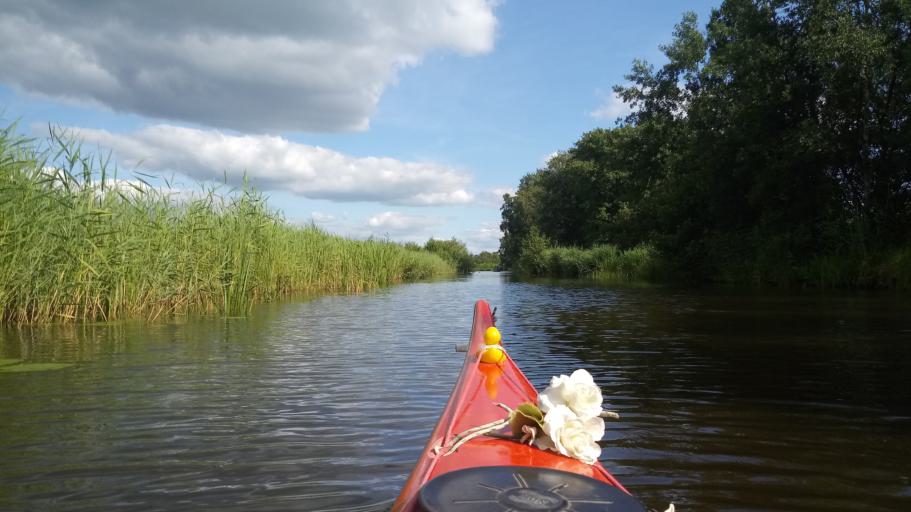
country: NL
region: Overijssel
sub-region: Gemeente Steenwijkerland
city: Wanneperveen
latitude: 52.7242
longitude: 6.1163
